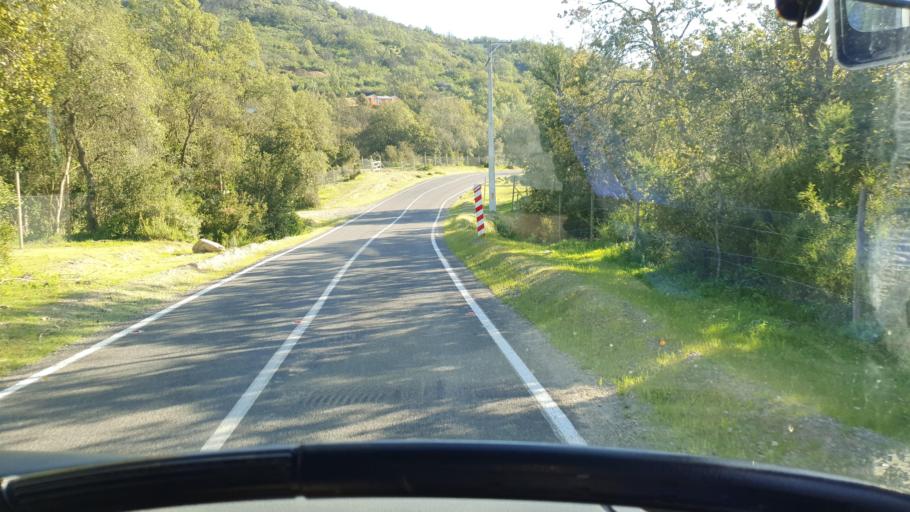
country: CL
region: Valparaiso
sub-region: Provincia de Marga Marga
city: Limache
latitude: -33.2027
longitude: -71.2431
